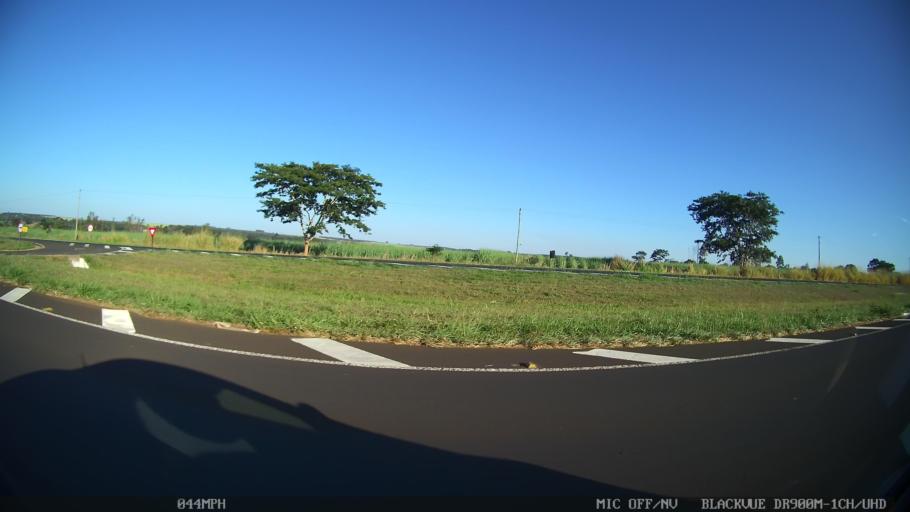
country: BR
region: Sao Paulo
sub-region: Guapiacu
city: Guapiacu
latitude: -20.7643
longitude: -49.1907
